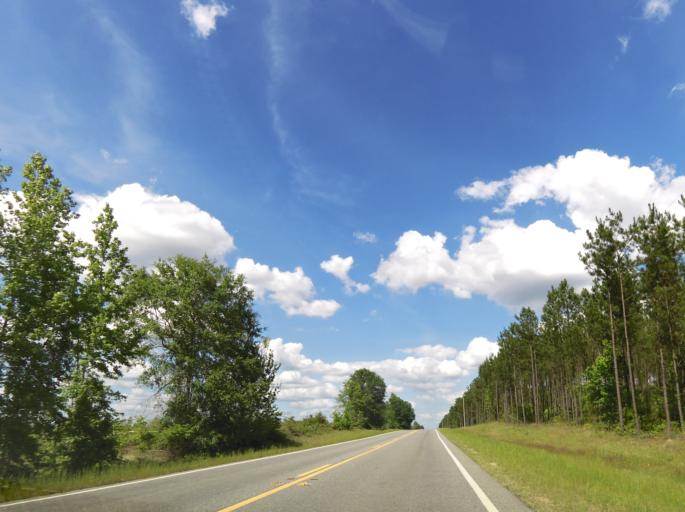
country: US
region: Georgia
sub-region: Wheeler County
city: Alamo
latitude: 32.2778
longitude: -82.7092
